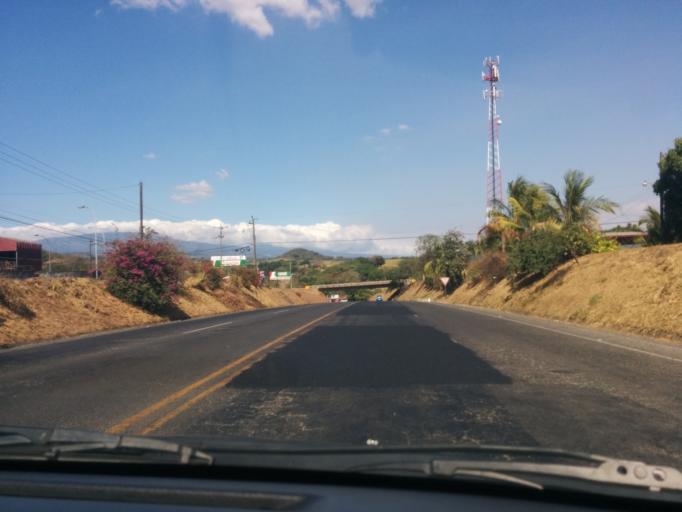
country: CR
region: Alajuela
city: Atenas
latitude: 10.0156
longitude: -84.3446
